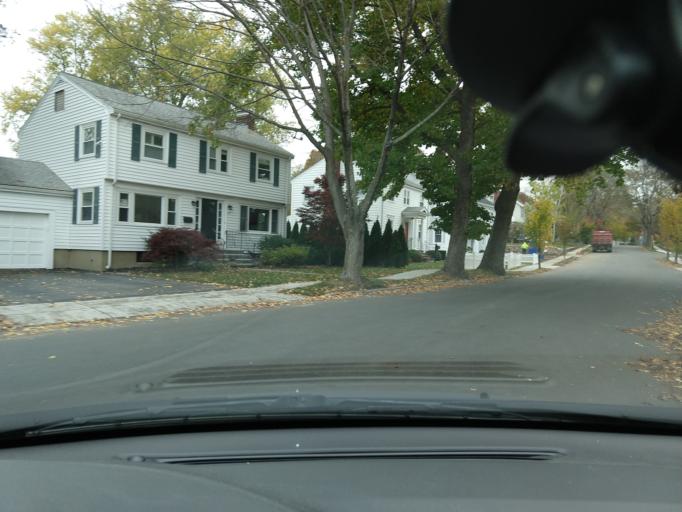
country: US
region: Massachusetts
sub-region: Middlesex County
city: Belmont
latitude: 42.4010
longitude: -71.1657
